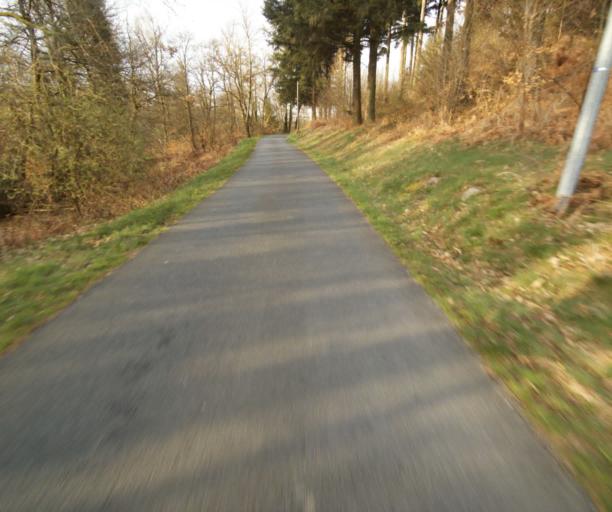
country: FR
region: Limousin
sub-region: Departement de la Correze
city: Correze
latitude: 45.4027
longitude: 1.8721
